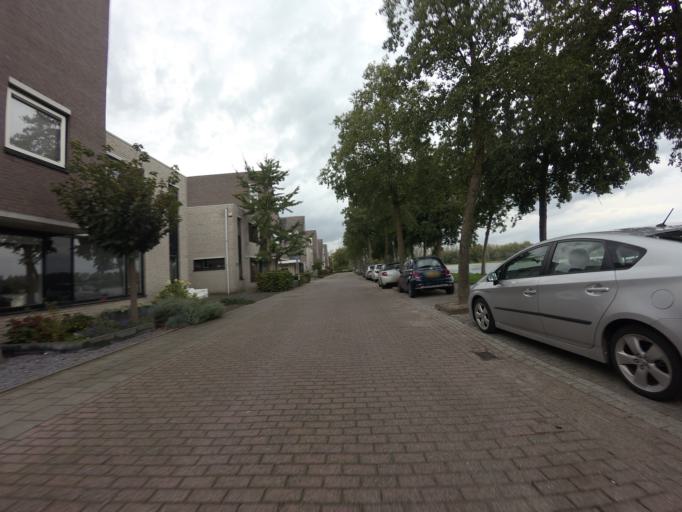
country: NL
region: North Brabant
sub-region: Gemeente Breda
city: Hoge Vucht
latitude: 51.6252
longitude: 4.7507
